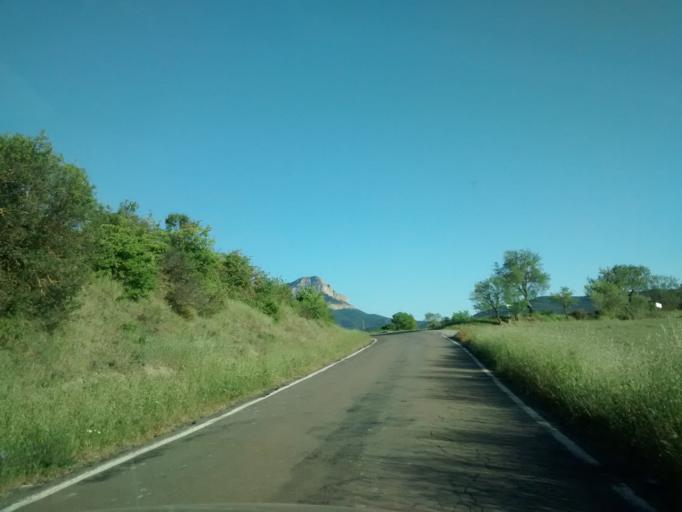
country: ES
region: Aragon
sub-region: Provincia de Huesca
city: Jaca
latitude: 42.5821
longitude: -0.5851
